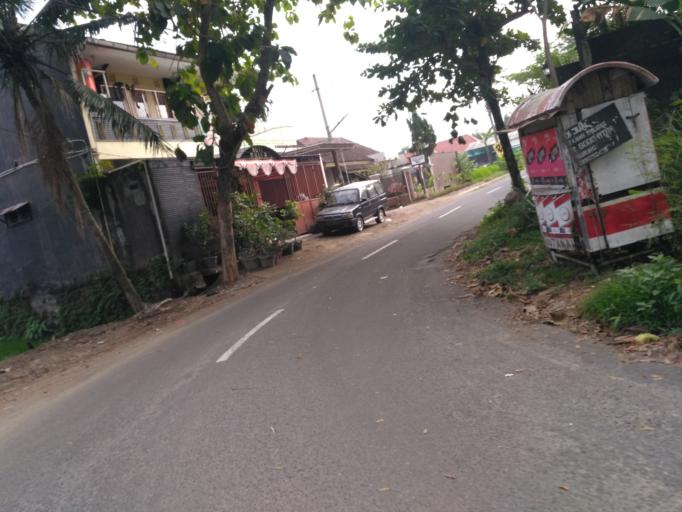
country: ID
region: Daerah Istimewa Yogyakarta
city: Melati
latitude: -7.7195
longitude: 110.3986
